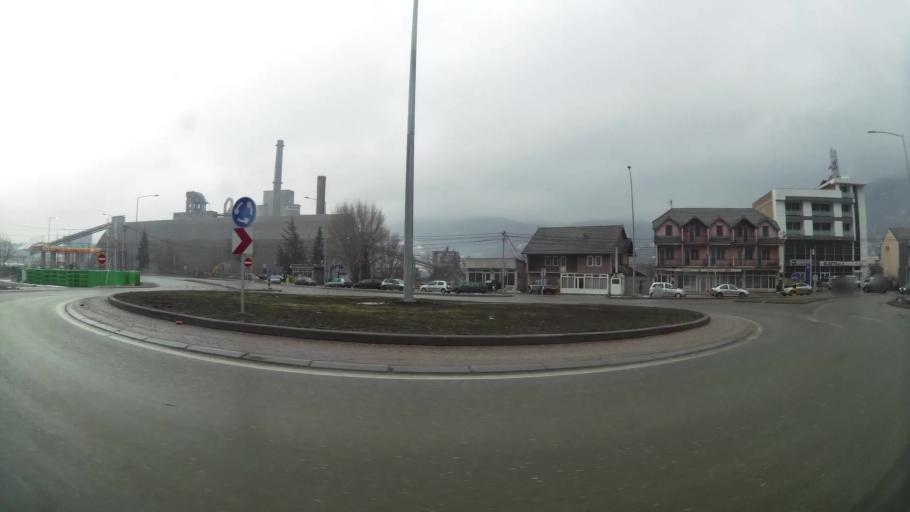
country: XK
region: Ferizaj
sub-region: Hani i Elezit
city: Hani i Elezit
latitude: 42.1499
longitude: 21.2995
